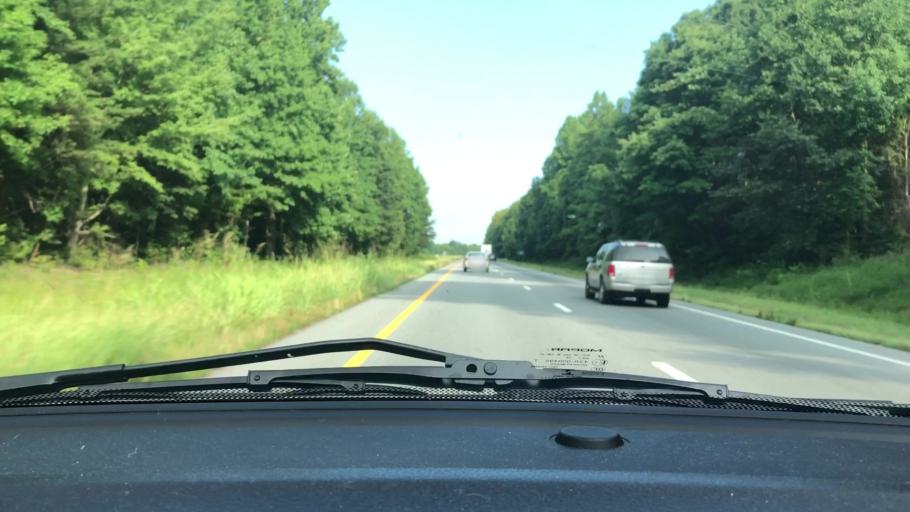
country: US
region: North Carolina
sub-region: Randolph County
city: Liberty
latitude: 35.8583
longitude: -79.6167
